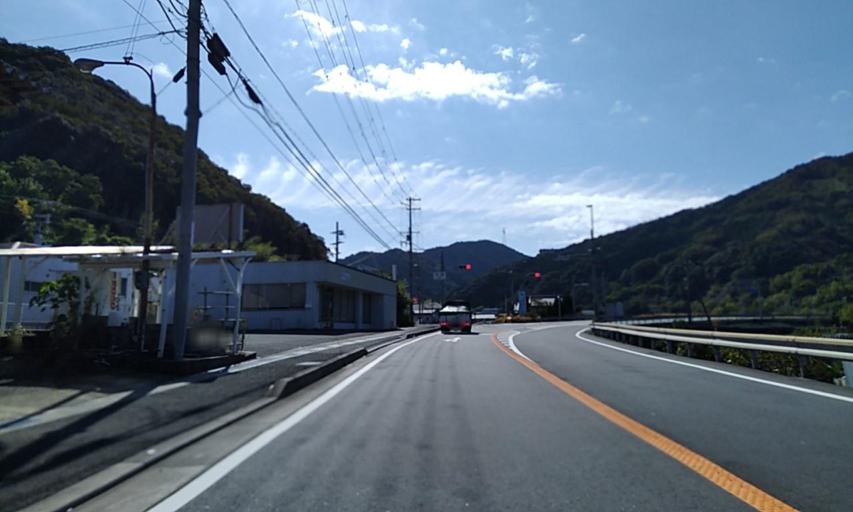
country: JP
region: Wakayama
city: Gobo
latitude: 34.0044
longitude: 135.1917
